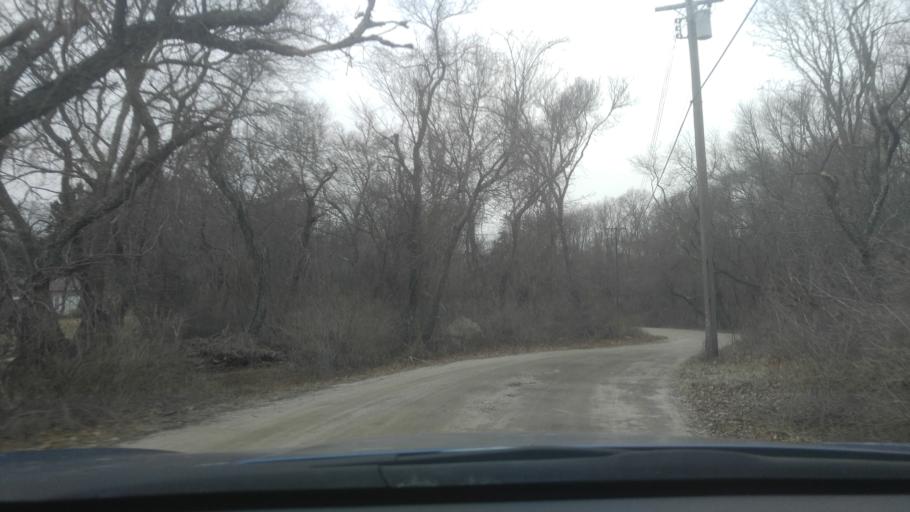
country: US
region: Rhode Island
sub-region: Washington County
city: Wakefield-Peacedale
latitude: 41.4123
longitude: -71.5263
